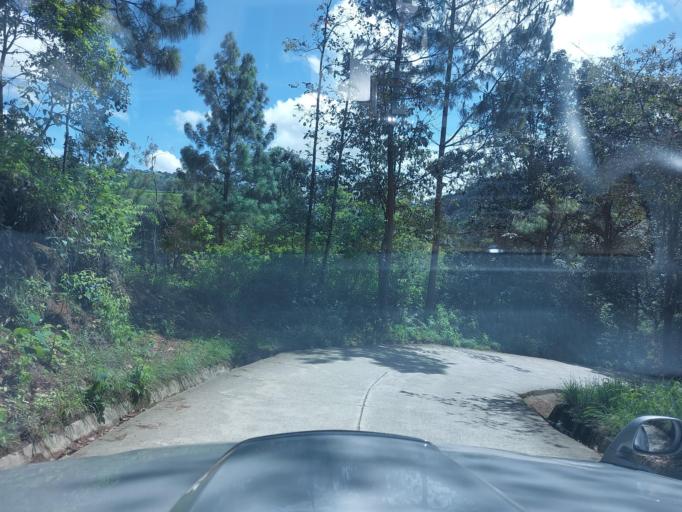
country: GT
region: Chimaltenango
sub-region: Municipio de San Juan Comalapa
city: Comalapa
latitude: 14.7558
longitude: -90.8731
